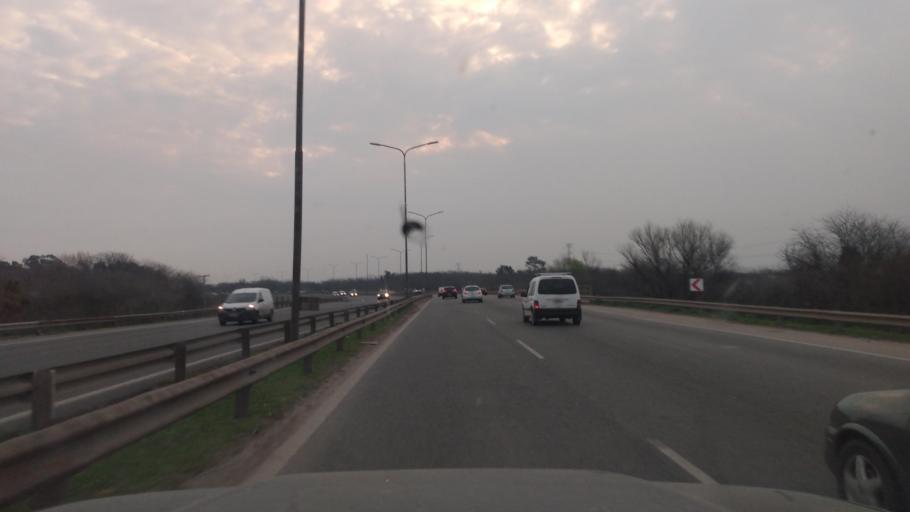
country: AR
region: Buenos Aires
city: Hurlingham
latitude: -34.5517
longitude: -58.6198
